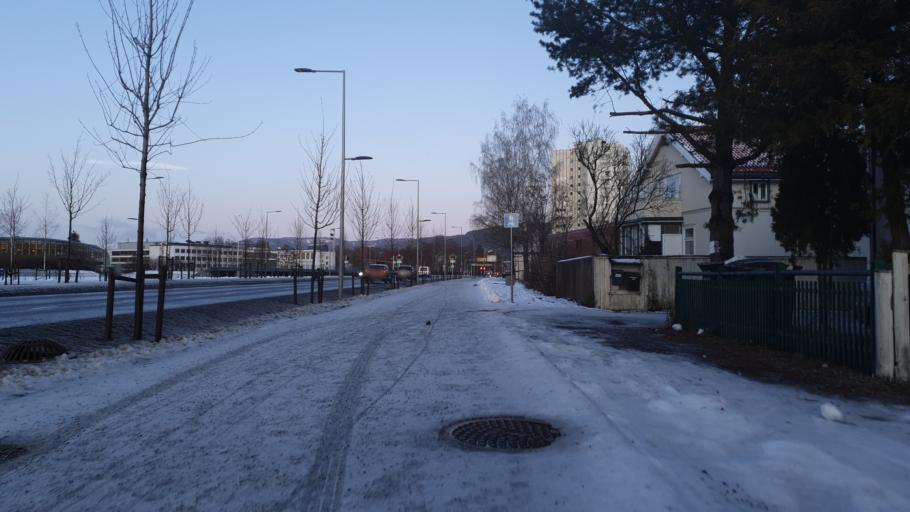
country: NO
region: Buskerud
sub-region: Drammen
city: Drammen
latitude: 59.7357
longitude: 10.2053
